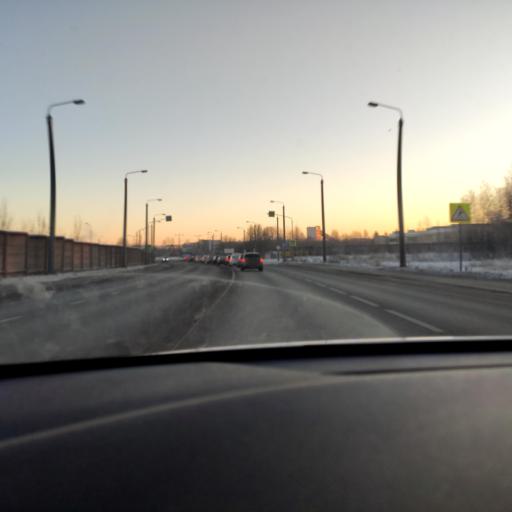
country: RU
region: Tatarstan
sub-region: Gorod Kazan'
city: Kazan
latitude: 55.8512
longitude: 49.1259
